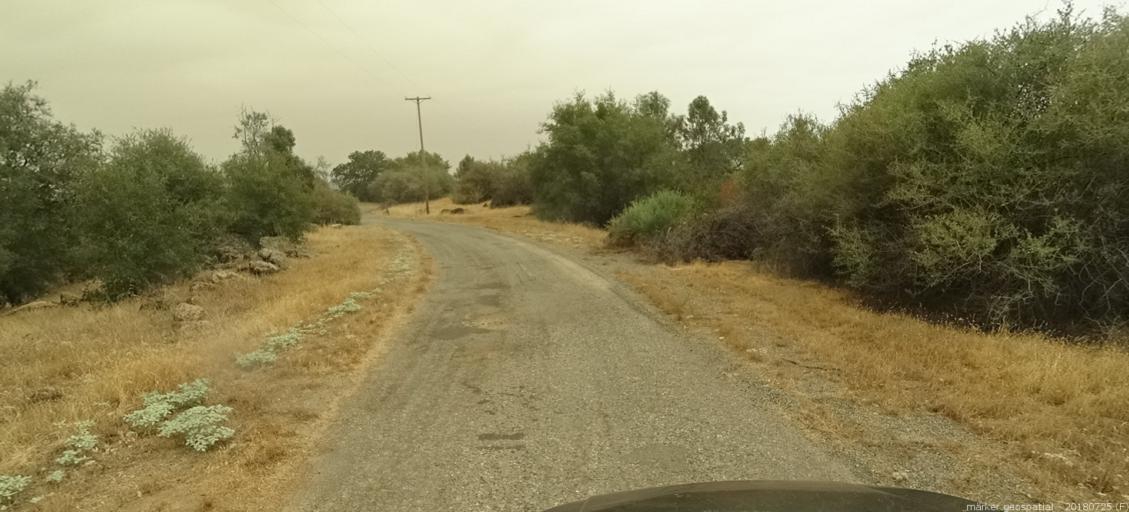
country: US
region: California
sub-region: Madera County
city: Yosemite Lakes
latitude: 37.1709
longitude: -119.6829
